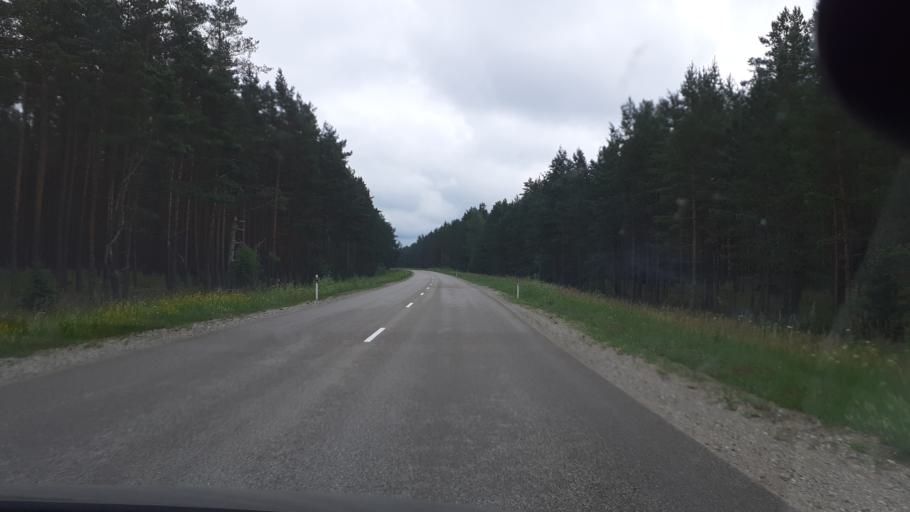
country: LV
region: Ventspils Rajons
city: Piltene
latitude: 57.1207
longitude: 21.7446
